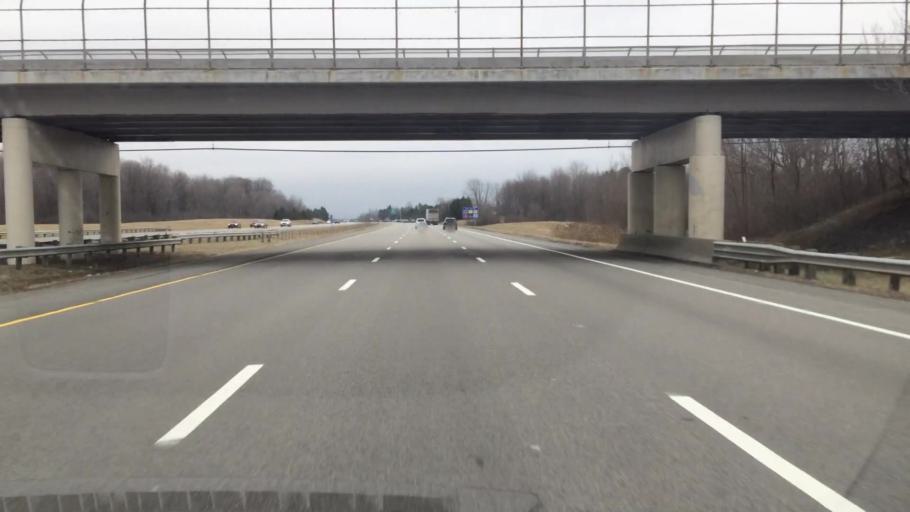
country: US
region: Ohio
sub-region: Medina County
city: Brunswick
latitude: 41.2614
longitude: -81.8047
